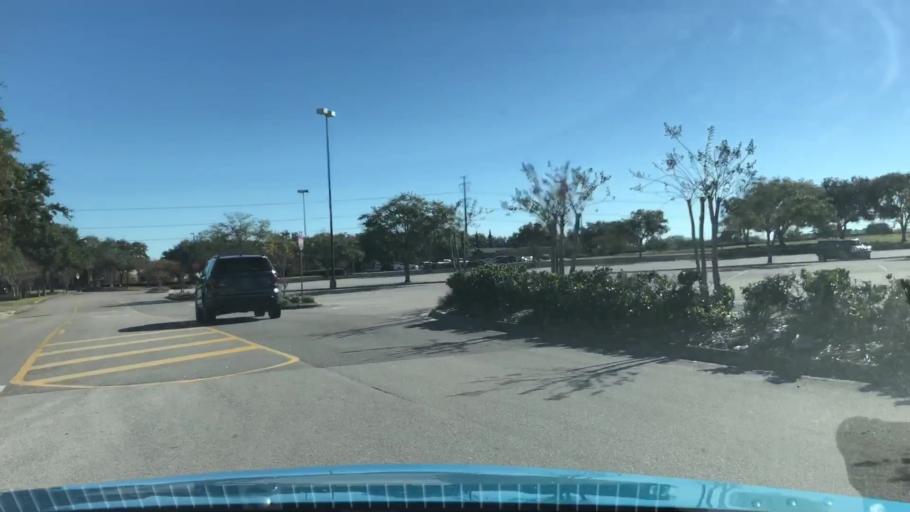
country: US
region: Florida
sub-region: Seminole County
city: Lake Mary
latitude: 28.8071
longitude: -81.3377
